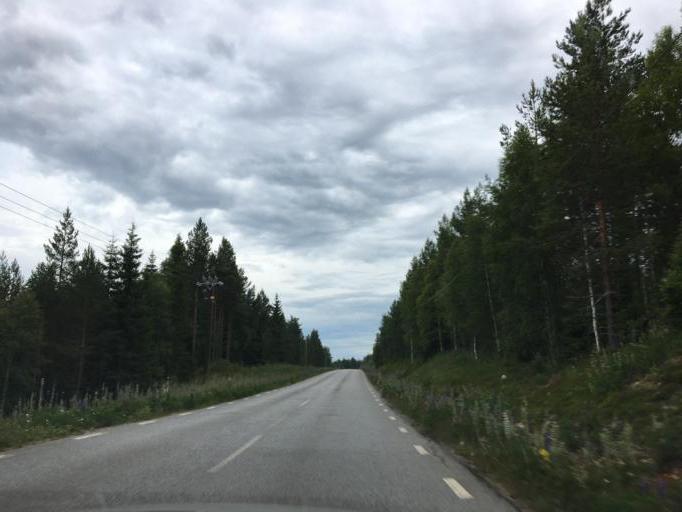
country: SE
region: Vaermland
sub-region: Filipstads Kommun
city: Lesjofors
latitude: 60.1650
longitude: 14.4049
